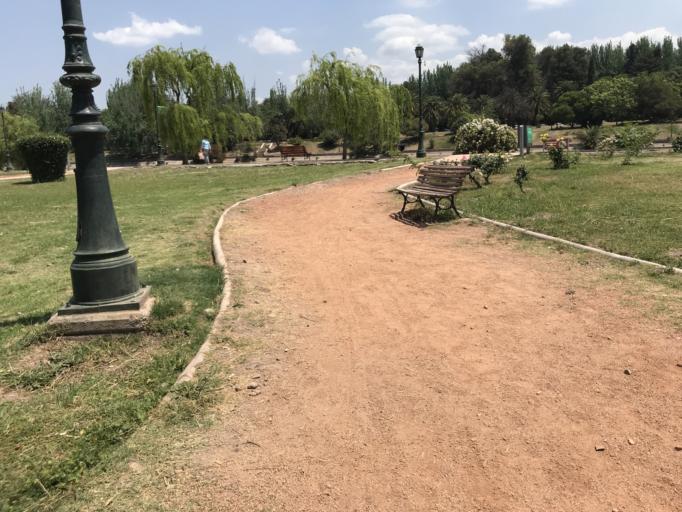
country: AR
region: Mendoza
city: Mendoza
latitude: -32.8905
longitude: -68.8671
